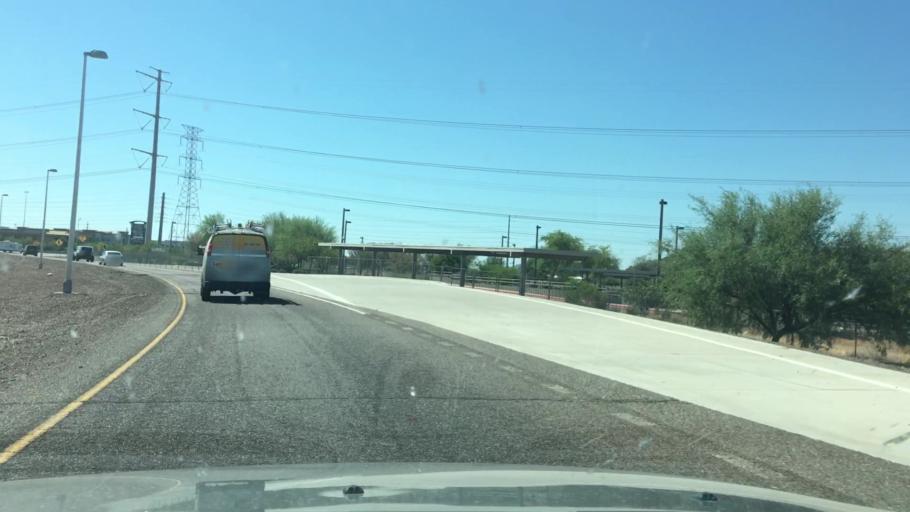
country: US
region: Arizona
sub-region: Maricopa County
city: Anthem
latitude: 33.7113
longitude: -112.1195
